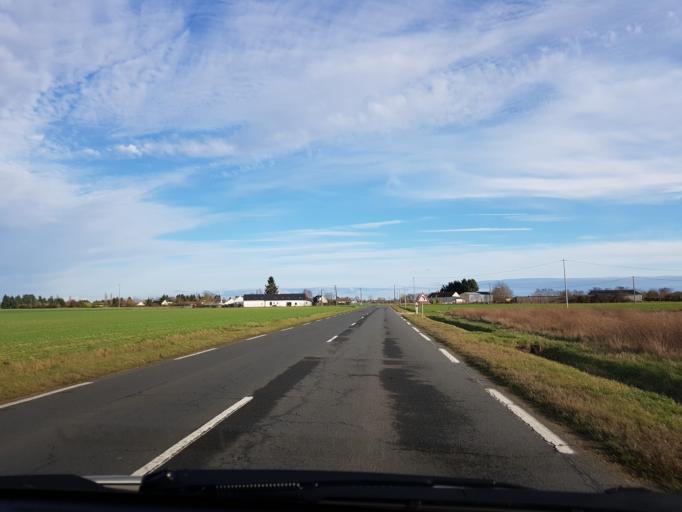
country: FR
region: Centre
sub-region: Departement du Loiret
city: Darvoy
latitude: 47.8505
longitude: 2.0669
